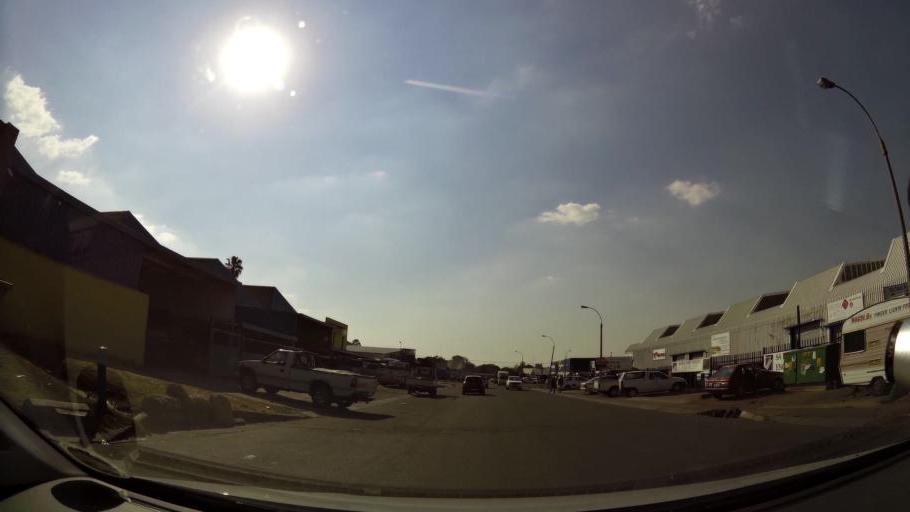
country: ZA
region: Gauteng
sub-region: City of Johannesburg Metropolitan Municipality
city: Modderfontein
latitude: -26.1134
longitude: 28.2172
